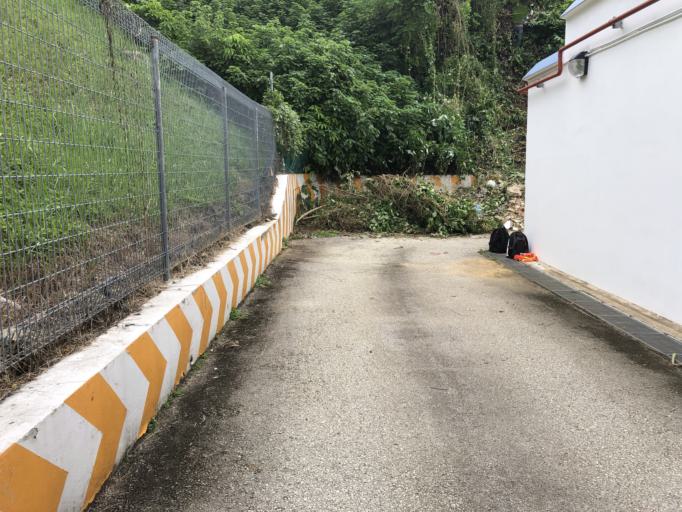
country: MY
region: Johor
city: Johor Bahru
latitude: 1.3606
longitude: 103.7675
